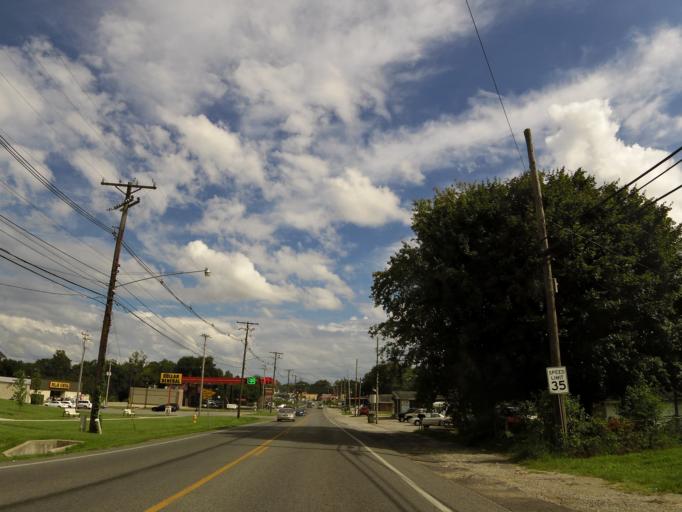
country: US
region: Kentucky
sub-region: Christian County
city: Hopkinsville
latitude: 36.8746
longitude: -87.5029
